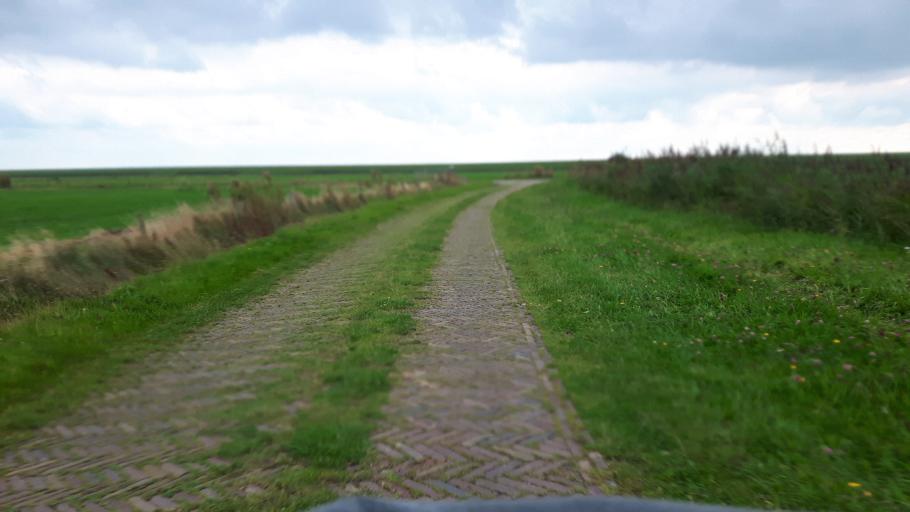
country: NL
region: Friesland
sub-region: Gemeente Ameland
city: Nes
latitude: 53.4445
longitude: 5.8214
